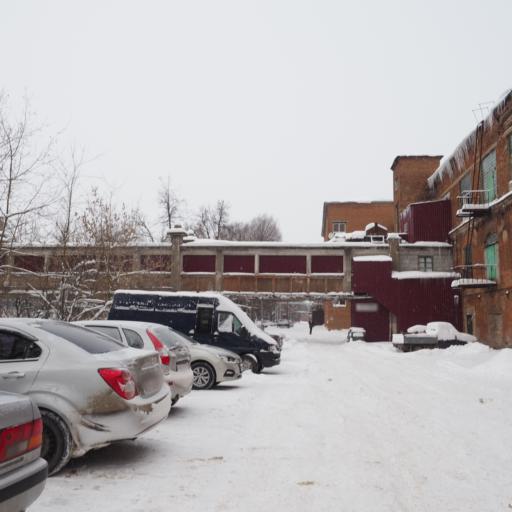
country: RU
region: Moskovskaya
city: Yegor'yevsk
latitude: 55.3859
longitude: 39.0227
